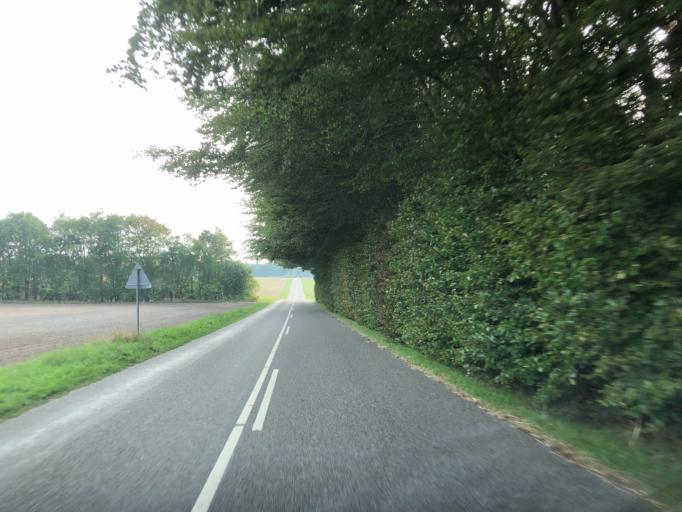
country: DK
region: Central Jutland
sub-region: Ringkobing-Skjern Kommune
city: Videbaek
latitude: 56.0698
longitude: 8.6967
